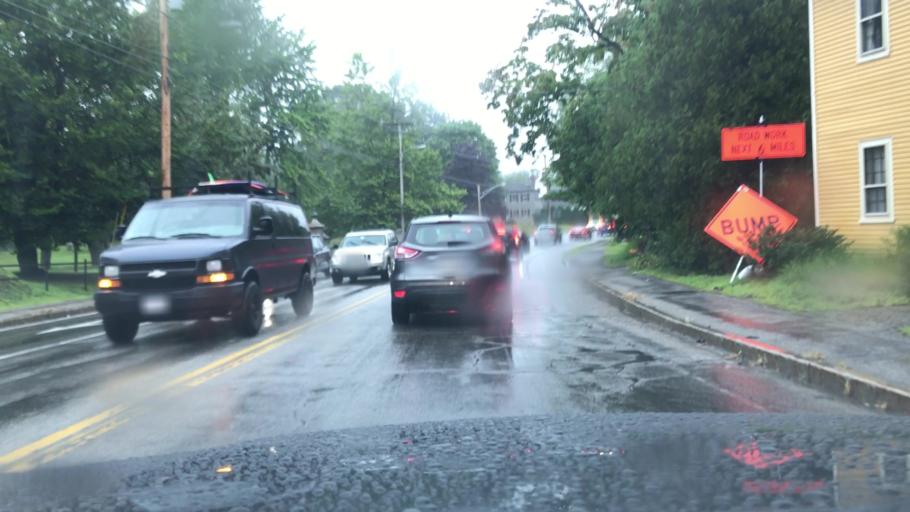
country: US
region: Maine
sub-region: York County
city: Kennebunk
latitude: 43.3882
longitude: -70.5369
